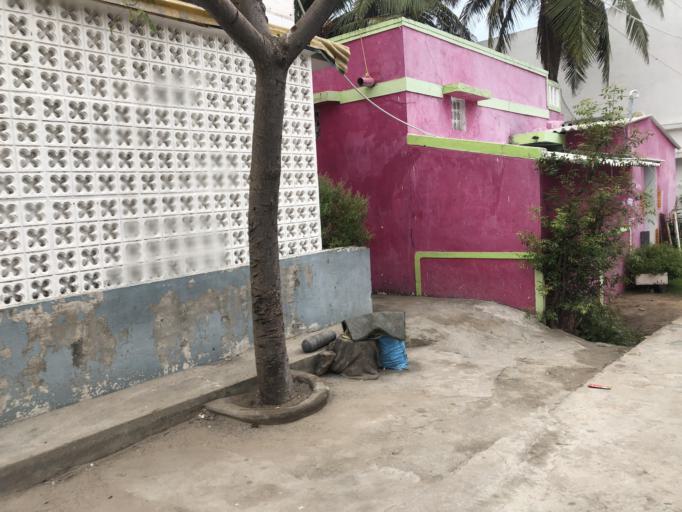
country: IN
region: Tamil Nadu
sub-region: Kancheepuram
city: Mamallapuram
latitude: 12.5973
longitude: 80.1902
